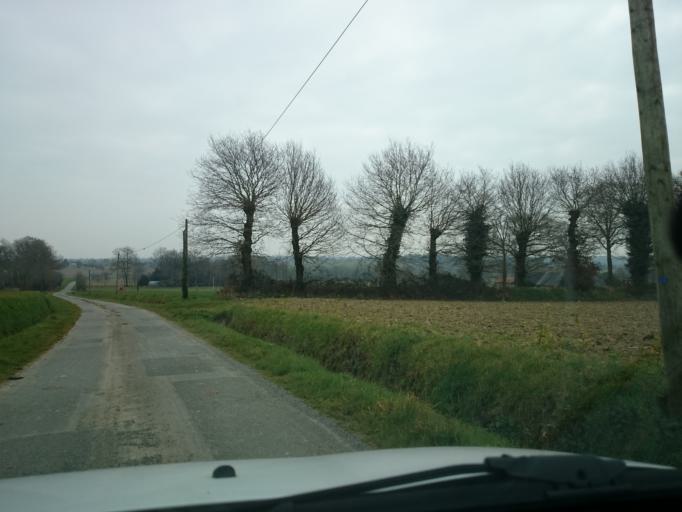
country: FR
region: Brittany
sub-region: Departement d'Ille-et-Vilaine
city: Tremblay
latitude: 48.4064
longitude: -1.5254
